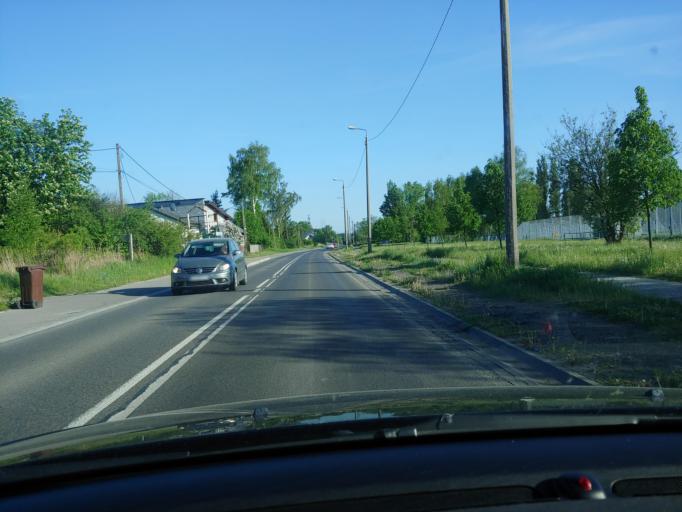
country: PL
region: Silesian Voivodeship
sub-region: Jaworzno
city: Jaworzno
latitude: 50.1886
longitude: 19.2868
